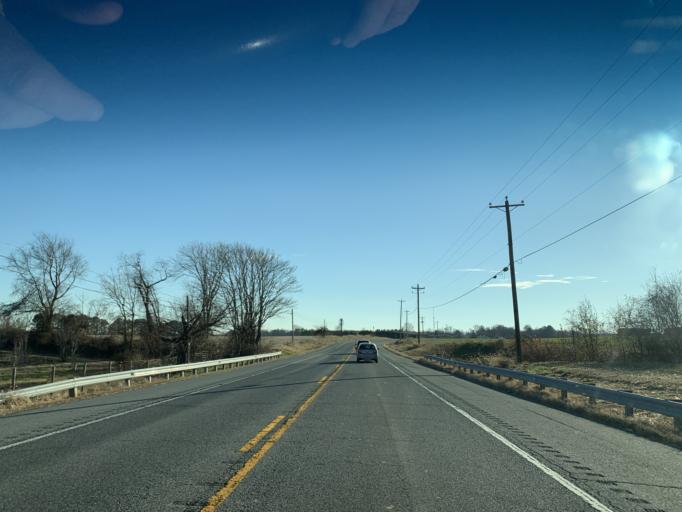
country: US
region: Delaware
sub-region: New Castle County
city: Middletown
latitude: 39.4179
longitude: -75.8611
